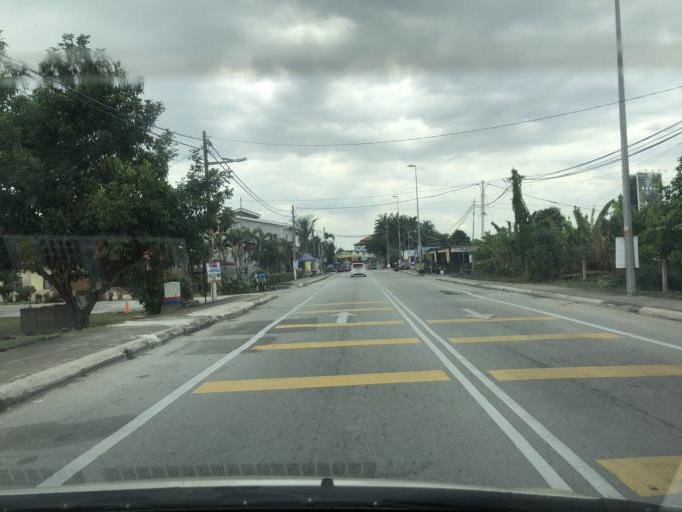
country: MY
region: Putrajaya
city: Putrajaya
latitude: 2.9221
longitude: 101.7586
